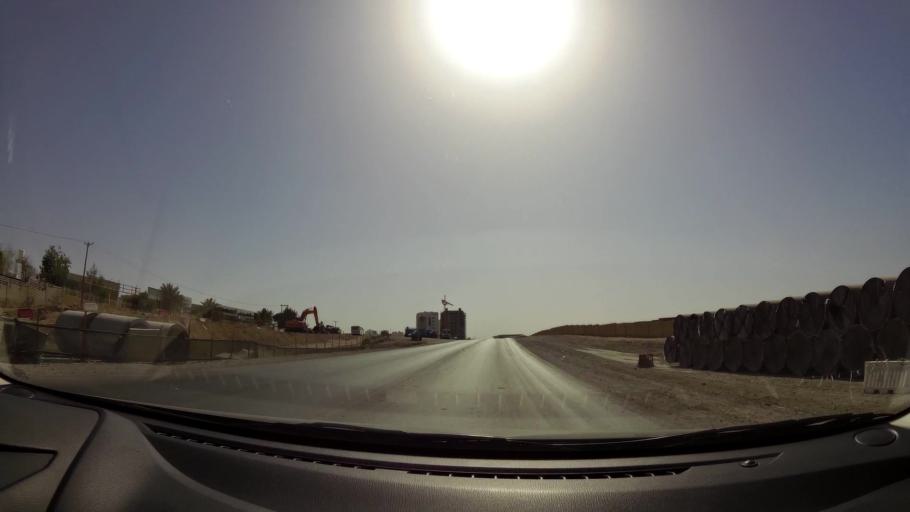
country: OM
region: Muhafazat Masqat
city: Bawshar
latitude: 23.5800
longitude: 58.3616
